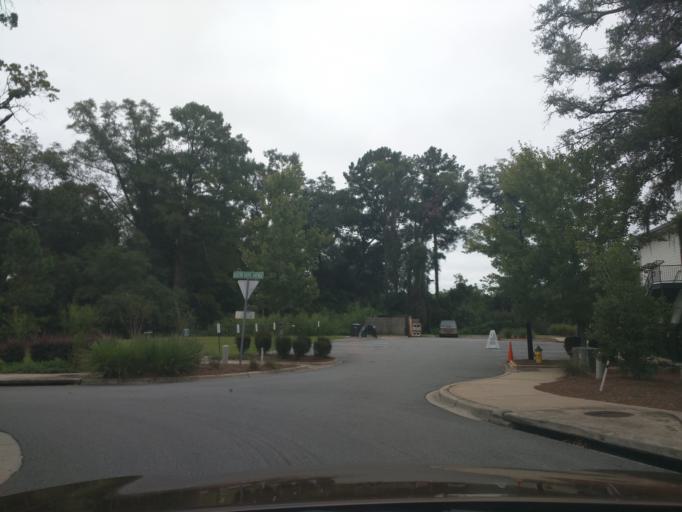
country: US
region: Florida
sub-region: Leon County
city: Tallahassee
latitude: 30.4624
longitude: -84.2295
